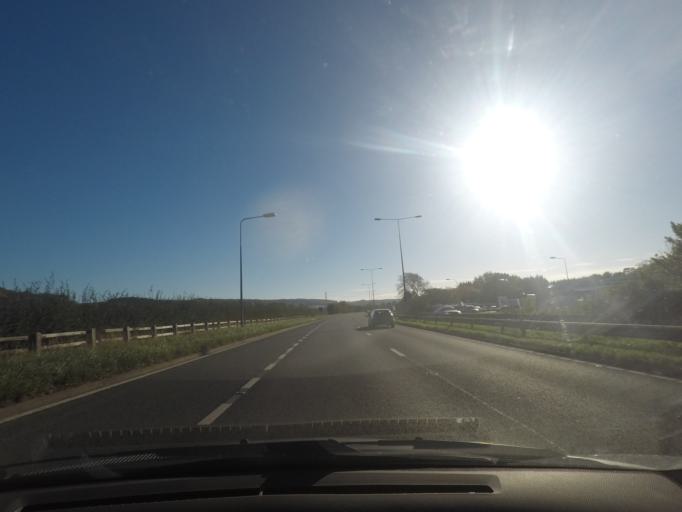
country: GB
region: England
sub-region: East Riding of Yorkshire
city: South Cave
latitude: 53.7607
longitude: -0.5944
